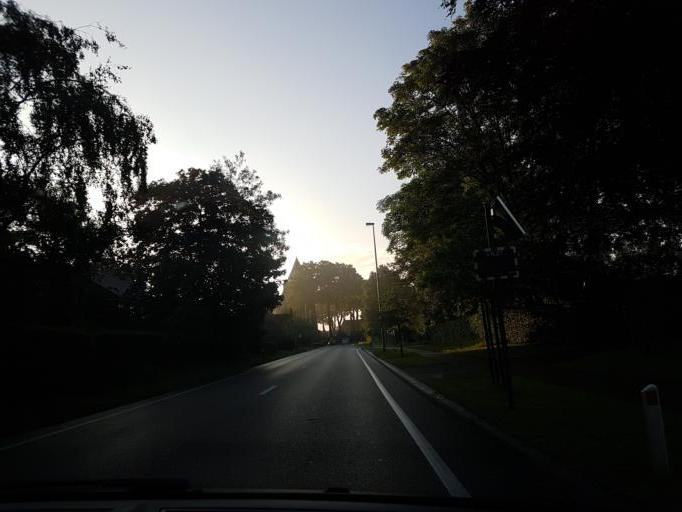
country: BE
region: Flanders
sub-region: Provincie Antwerpen
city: Hoogstraten
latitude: 51.3983
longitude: 4.7909
